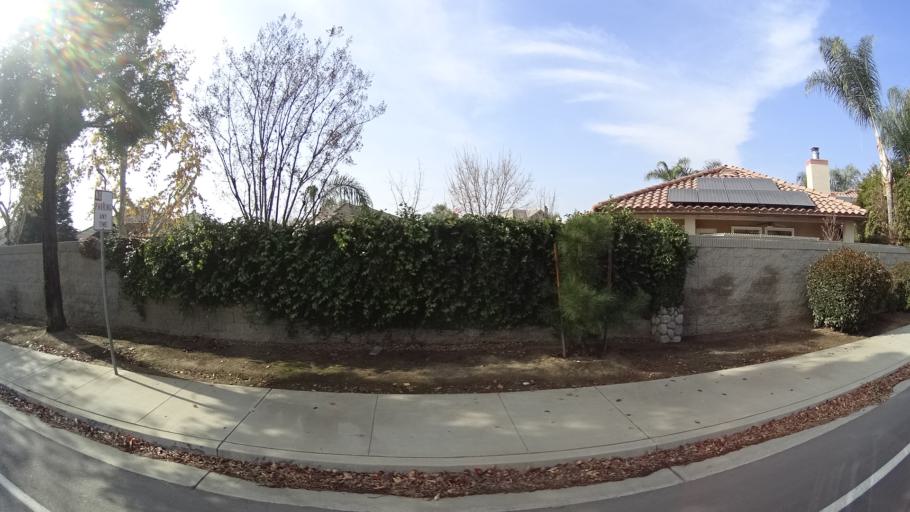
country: US
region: California
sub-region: Kern County
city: Greenacres
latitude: 35.4090
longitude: -119.1012
